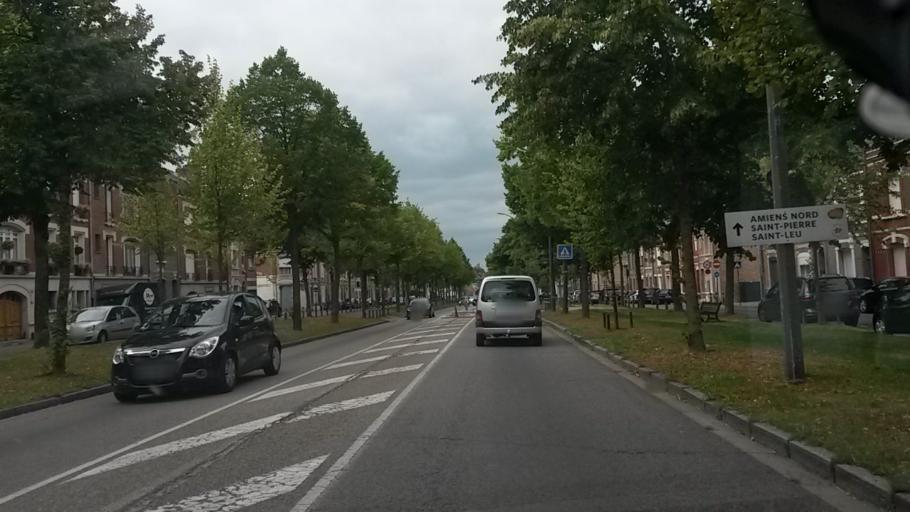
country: FR
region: Picardie
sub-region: Departement de la Somme
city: Amiens
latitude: 49.8849
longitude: 2.2809
